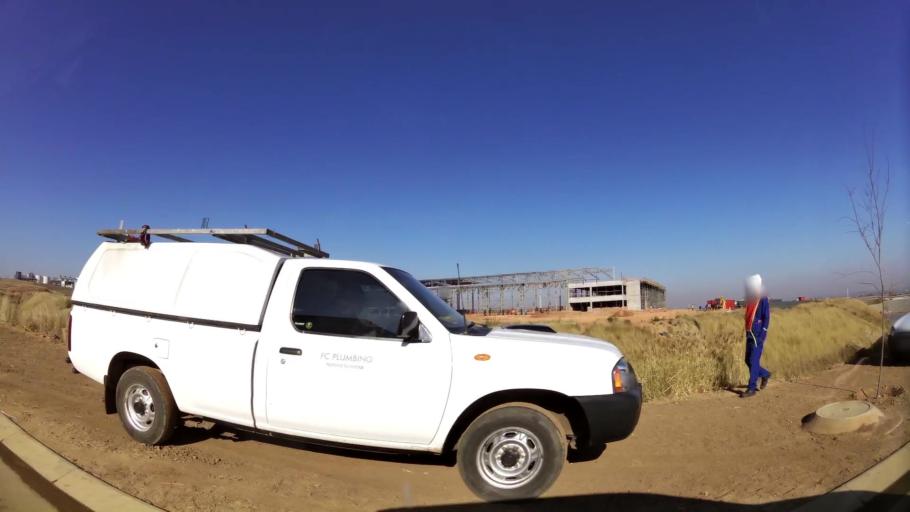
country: ZA
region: Gauteng
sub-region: City of Johannesburg Metropolitan Municipality
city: Modderfontein
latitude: -26.0472
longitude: 28.1656
